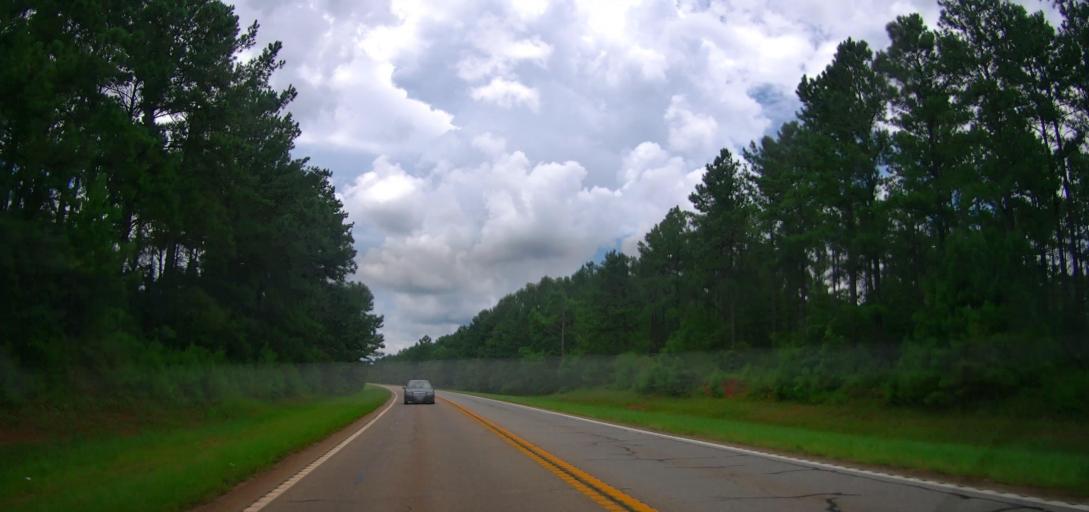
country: US
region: Georgia
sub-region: Pulaski County
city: Hawkinsville
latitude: 32.3567
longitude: -83.5365
